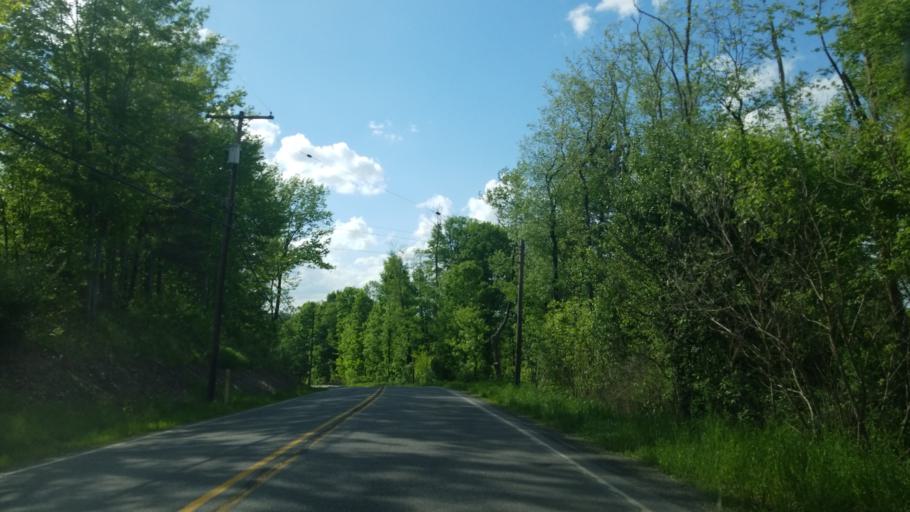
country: US
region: Pennsylvania
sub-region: Clearfield County
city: Troy
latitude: 40.9136
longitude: -78.2501
